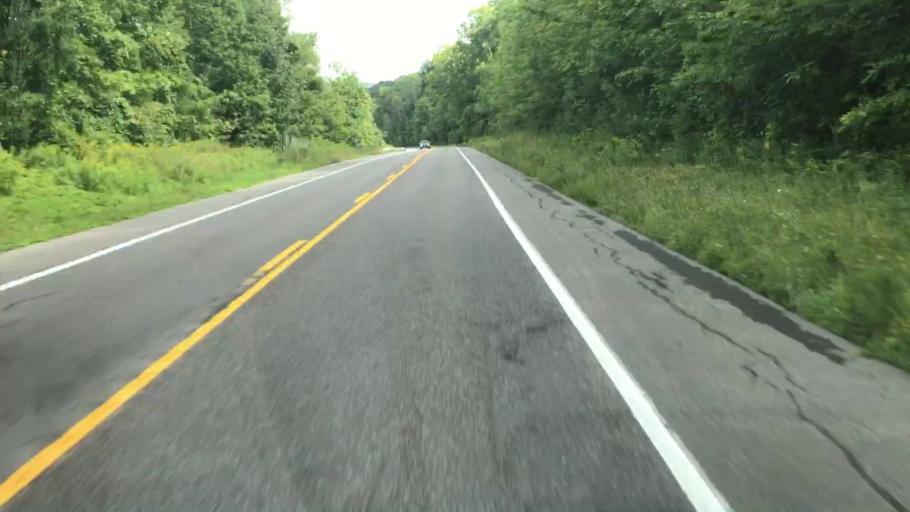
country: US
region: New York
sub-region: Onondaga County
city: Marcellus
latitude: 42.9520
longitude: -76.3600
